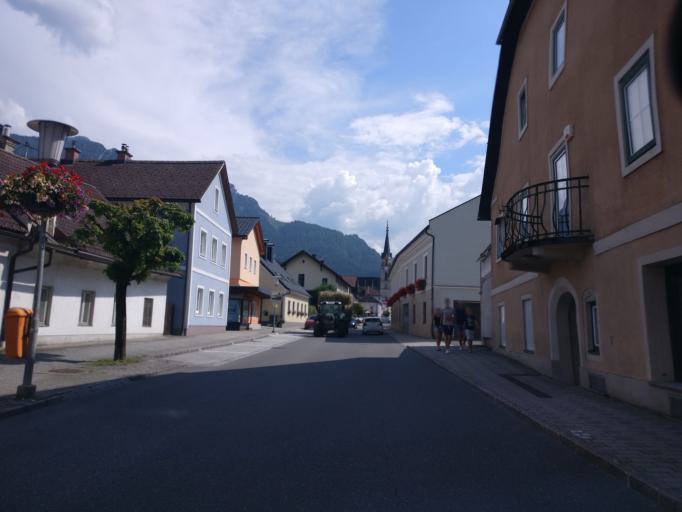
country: AT
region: Styria
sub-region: Politischer Bezirk Liezen
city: Admont
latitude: 47.5790
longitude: 14.4601
